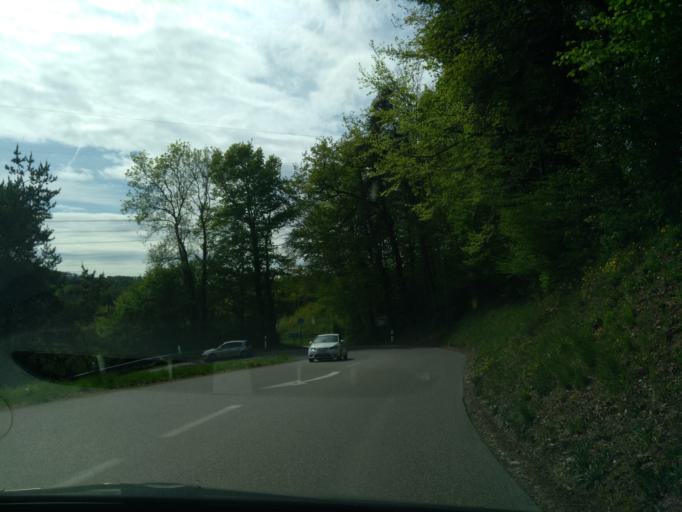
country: FR
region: Rhone-Alpes
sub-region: Departement de la Haute-Savoie
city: Chavanod
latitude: 45.8795
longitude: 6.0373
